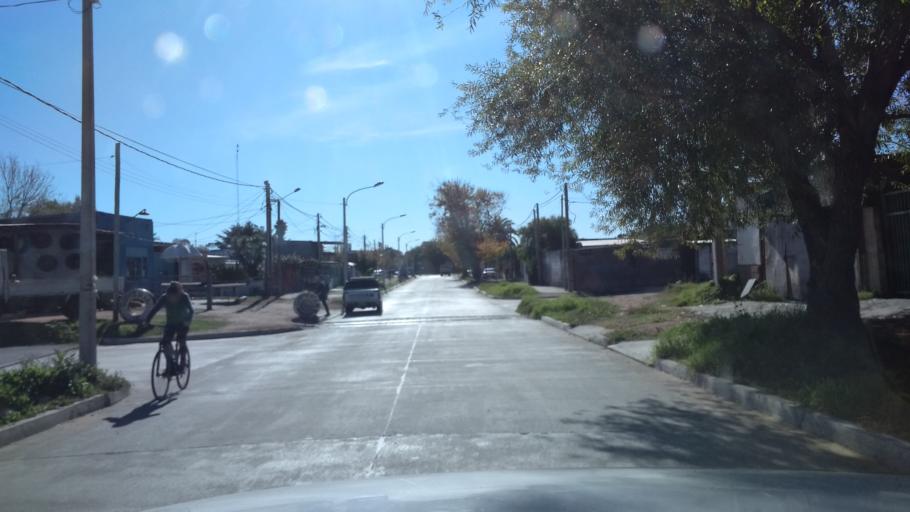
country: UY
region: Canelones
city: La Paz
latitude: -34.8266
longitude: -56.2245
